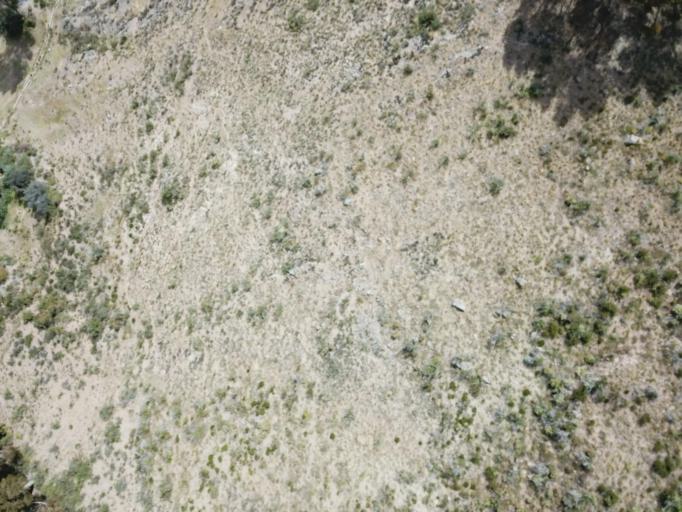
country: BO
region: La Paz
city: Achacachi
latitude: -16.0564
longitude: -68.8092
